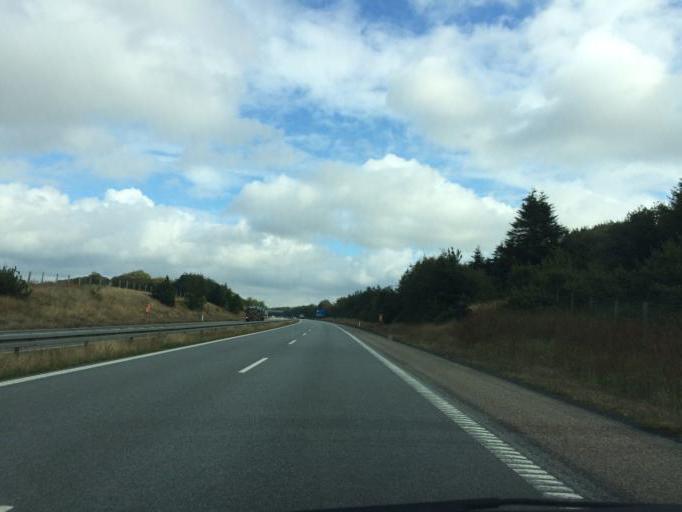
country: DK
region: North Denmark
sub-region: Bronderslev Kommune
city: Hjallerup
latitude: 57.1563
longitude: 10.1707
